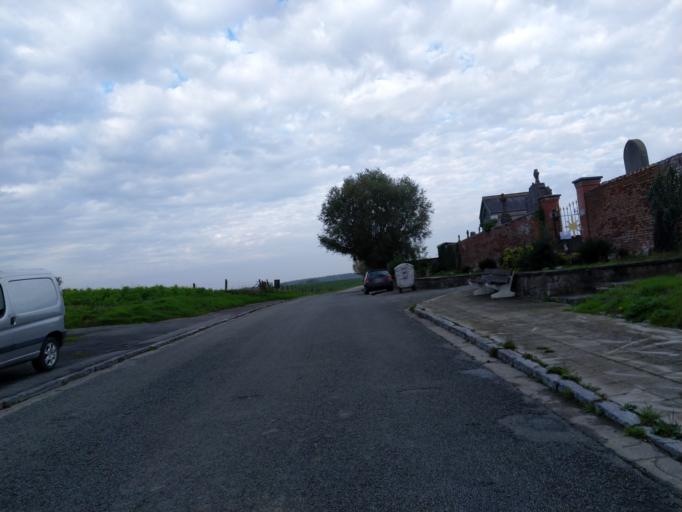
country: BE
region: Wallonia
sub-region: Province du Hainaut
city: Brugelette
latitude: 50.5968
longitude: 3.8472
